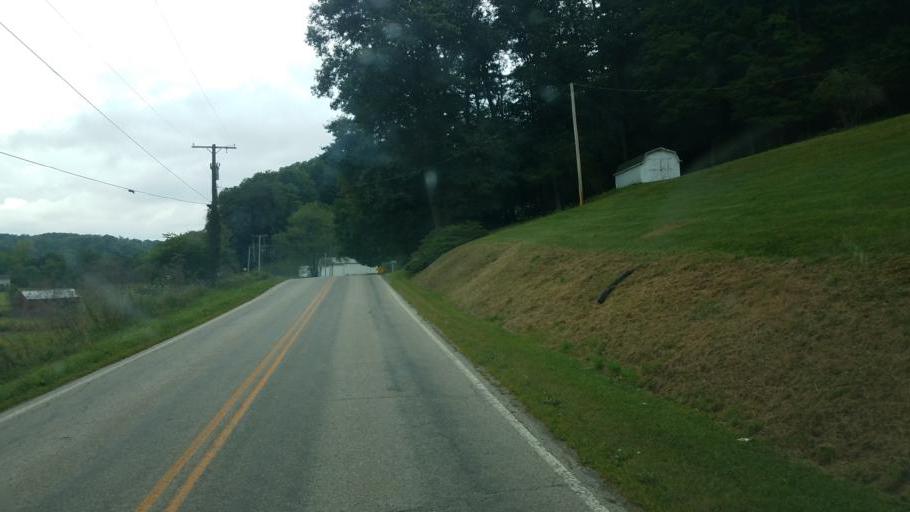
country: US
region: Ohio
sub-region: Sandusky County
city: Bellville
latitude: 40.6335
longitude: -82.4487
